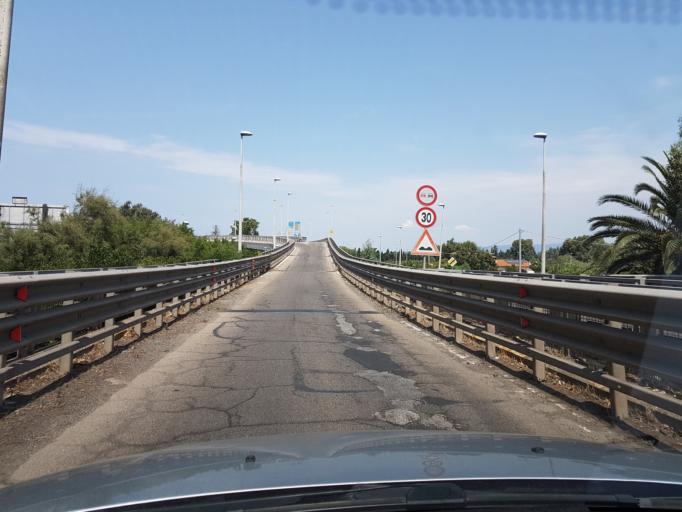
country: IT
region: Sardinia
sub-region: Provincia di Oristano
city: Donigala Fenugheddu
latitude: 39.9256
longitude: 8.5796
